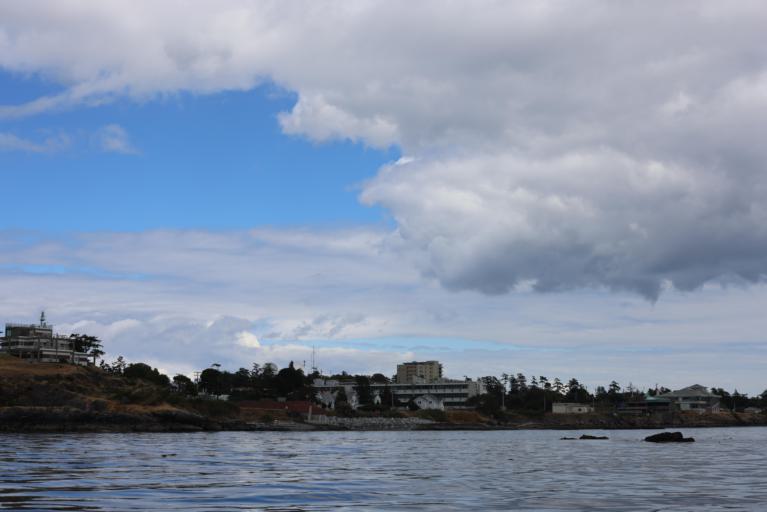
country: CA
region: British Columbia
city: Colwood
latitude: 48.4263
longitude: -123.4400
